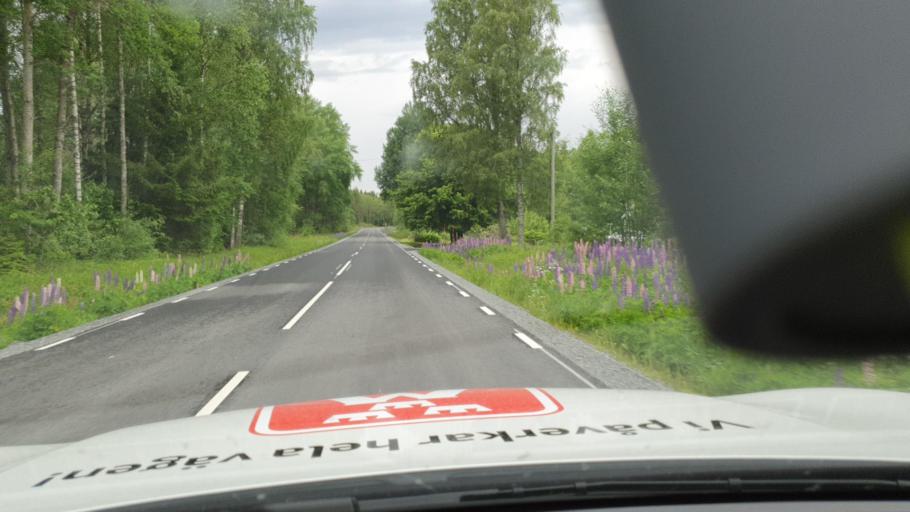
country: SE
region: Vaestra Goetaland
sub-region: Gullspangs Kommun
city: Anderstorp
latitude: 58.9151
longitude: 14.4521
